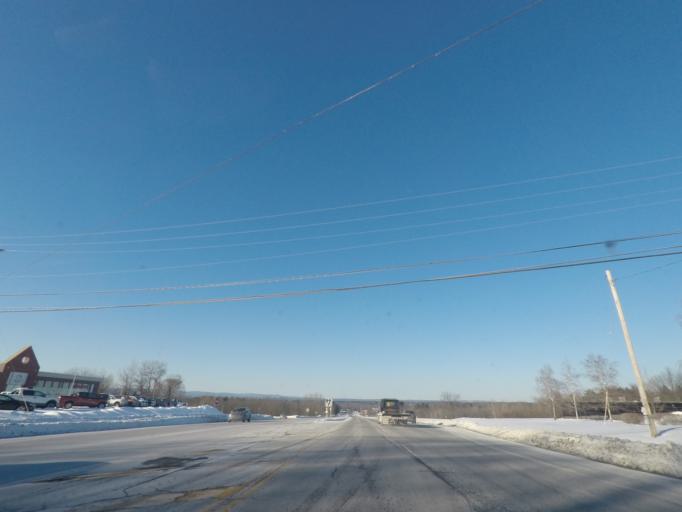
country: US
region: New York
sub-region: Saratoga County
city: North Ballston Spa
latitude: 43.0175
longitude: -73.7907
